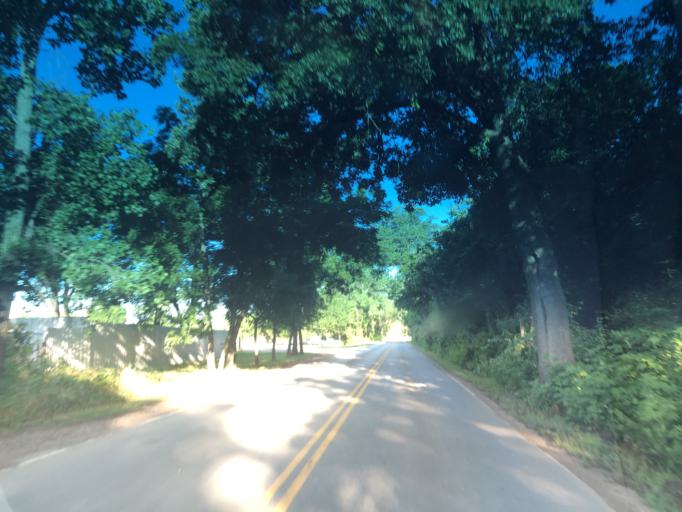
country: US
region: Texas
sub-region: Dallas County
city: Grand Prairie
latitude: 32.7924
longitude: -97.0024
